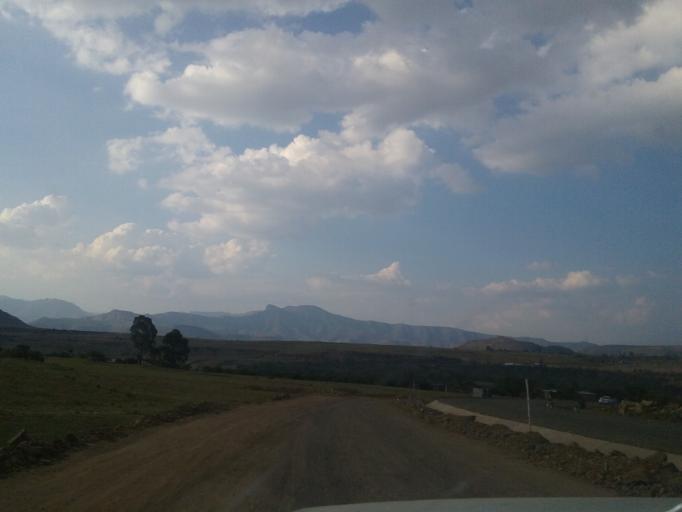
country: LS
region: Quthing
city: Quthing
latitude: -30.3971
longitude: 27.6124
